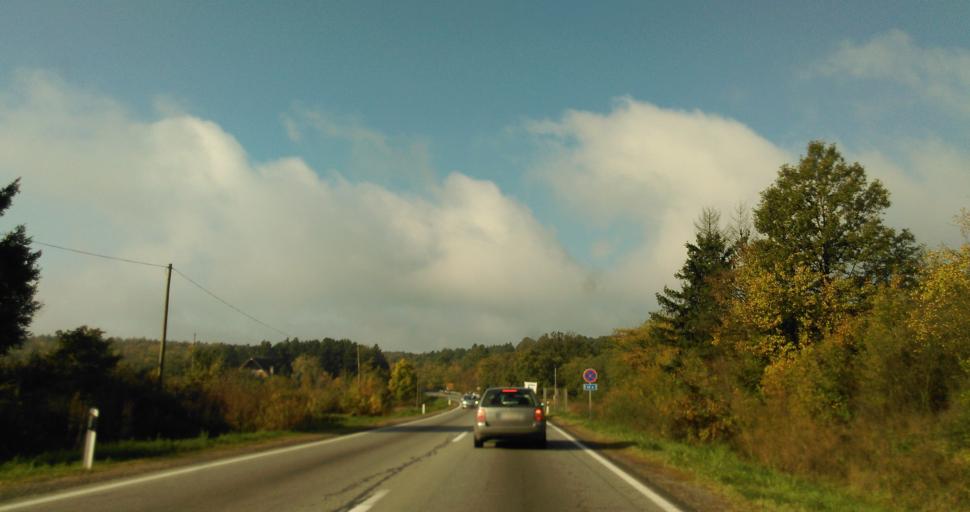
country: RS
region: Central Serbia
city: Sremcica
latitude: 44.6469
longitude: 20.4180
